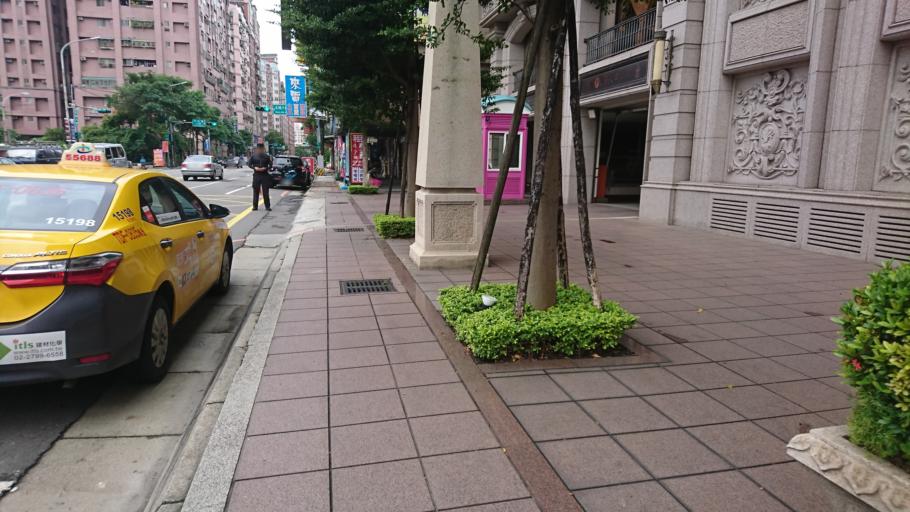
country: TW
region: Taiwan
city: Taoyuan City
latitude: 25.0545
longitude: 121.2993
